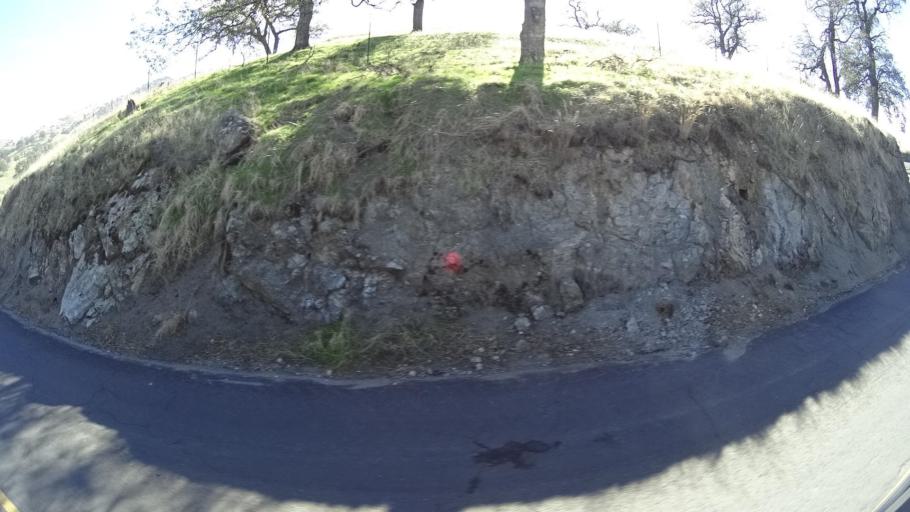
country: US
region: California
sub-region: Tulare County
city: Richgrove
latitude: 35.6987
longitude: -118.8578
